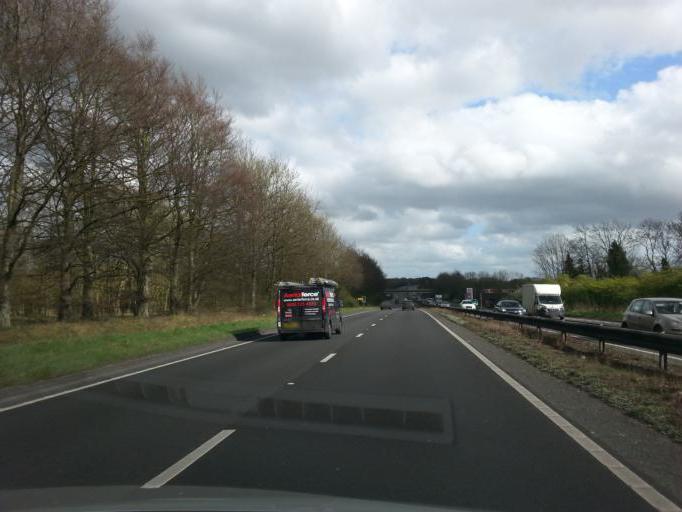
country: GB
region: England
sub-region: Hampshire
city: Andover
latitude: 51.1817
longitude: -1.3803
